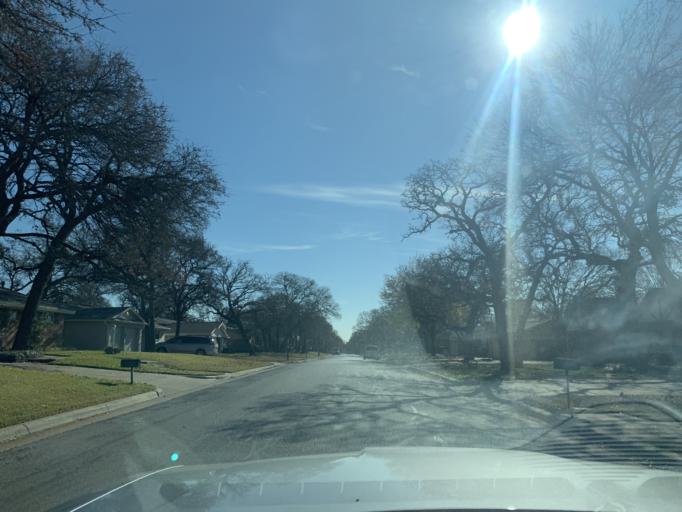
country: US
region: Texas
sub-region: Tarrant County
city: Bedford
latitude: 32.8478
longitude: -97.1510
